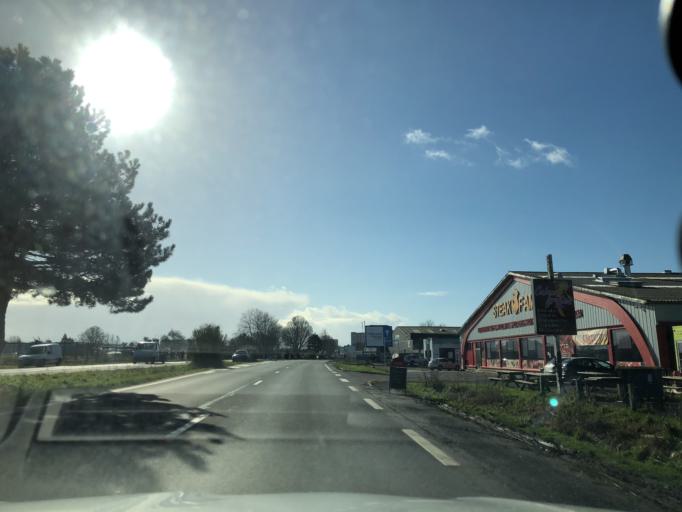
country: FR
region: Lower Normandy
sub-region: Departement du Calvados
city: Caen
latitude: 49.2095
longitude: -0.3458
